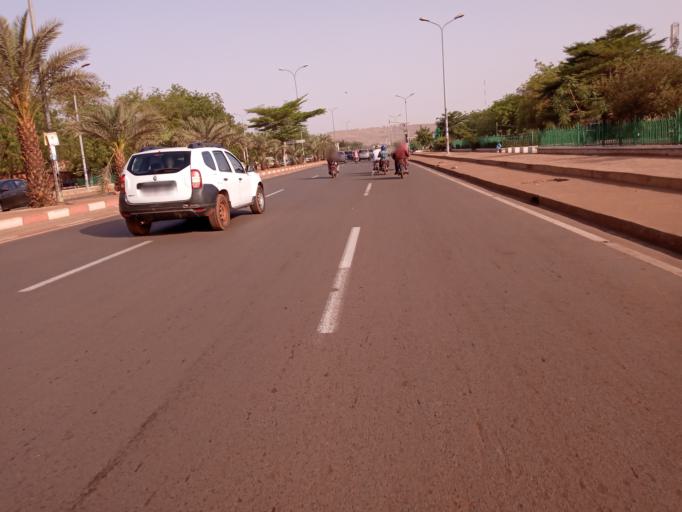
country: ML
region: Bamako
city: Bamako
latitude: 12.6396
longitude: -8.0060
